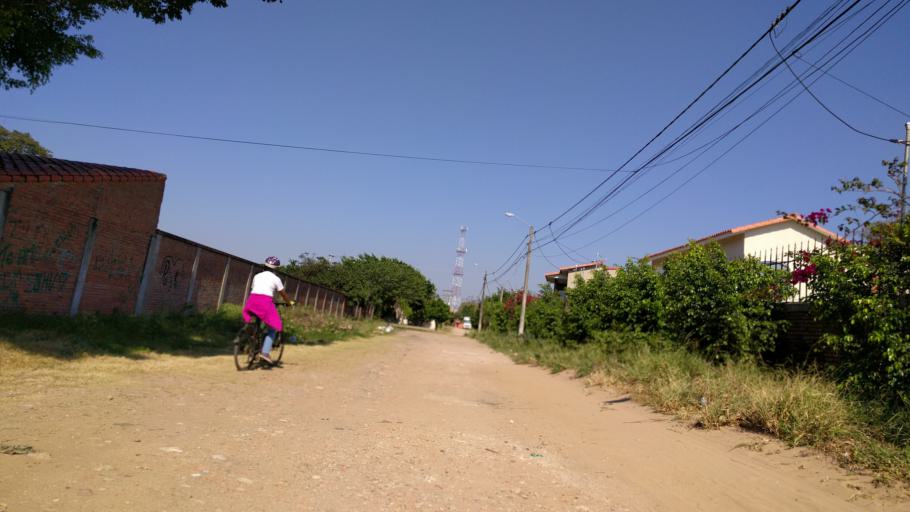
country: BO
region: Santa Cruz
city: Santa Cruz de la Sierra
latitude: -17.8138
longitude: -63.2280
